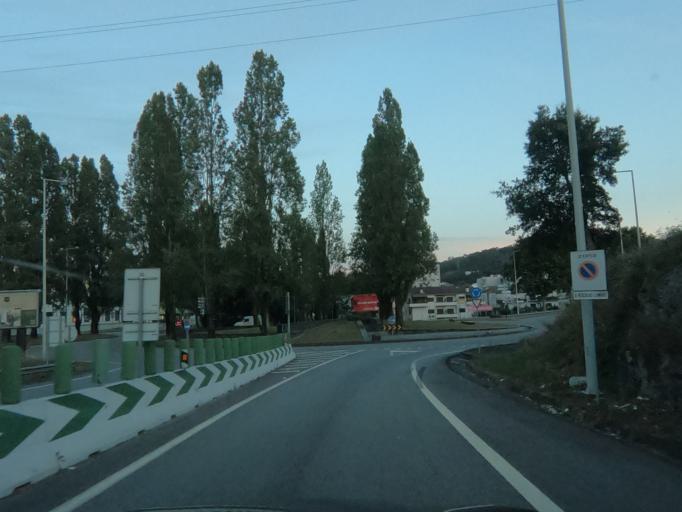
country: PT
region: Porto
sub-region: Valongo
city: Valongo
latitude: 41.1935
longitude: -8.5041
